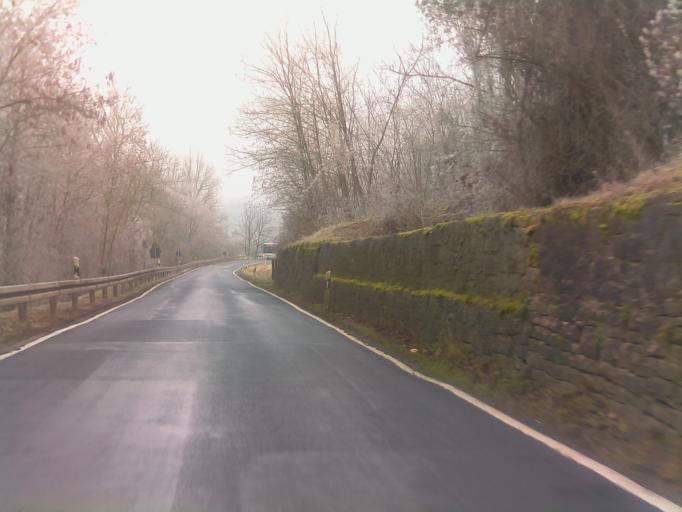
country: DE
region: Bavaria
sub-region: Regierungsbezirk Unterfranken
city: Marktsteft
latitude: 49.6840
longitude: 10.1379
